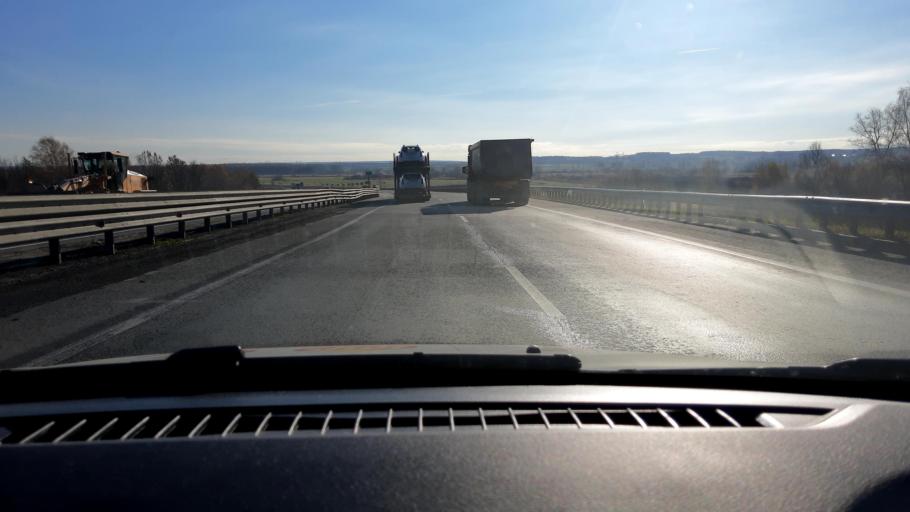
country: RU
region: Nizjnij Novgorod
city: Burevestnik
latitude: 56.1279
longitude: 43.7828
